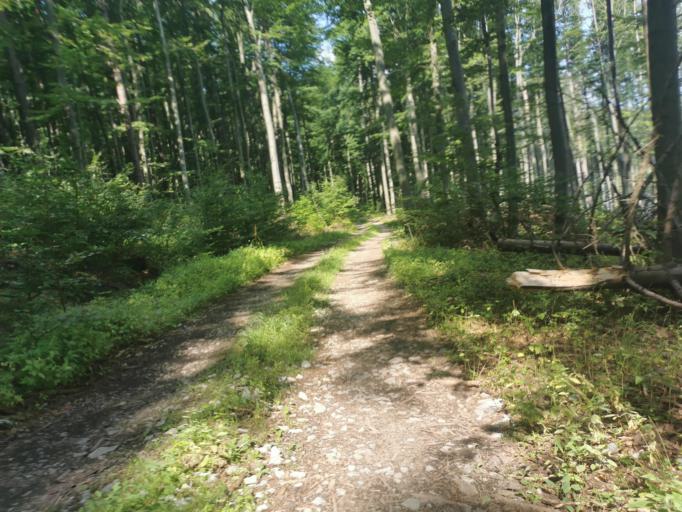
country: SK
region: Trenciansky
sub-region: Okres Myjava
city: Myjava
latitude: 48.8312
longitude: 17.5980
